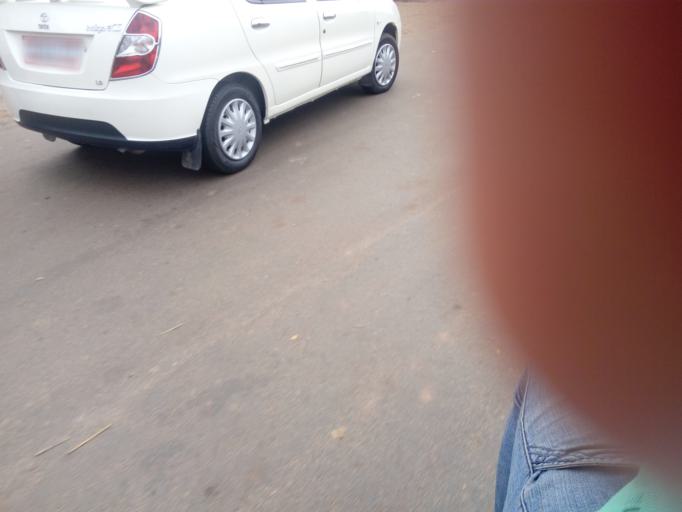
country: IN
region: Odisha
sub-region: Khordha
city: Bhubaneshwar
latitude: 20.2937
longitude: 85.8424
